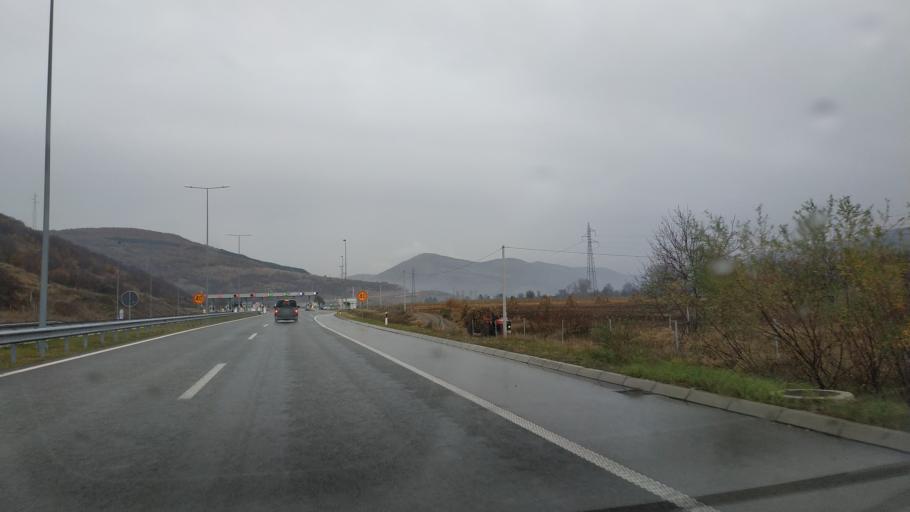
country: RS
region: Central Serbia
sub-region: Pirotski Okrug
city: Dimitrovgrad
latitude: 43.0217
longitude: 22.7326
